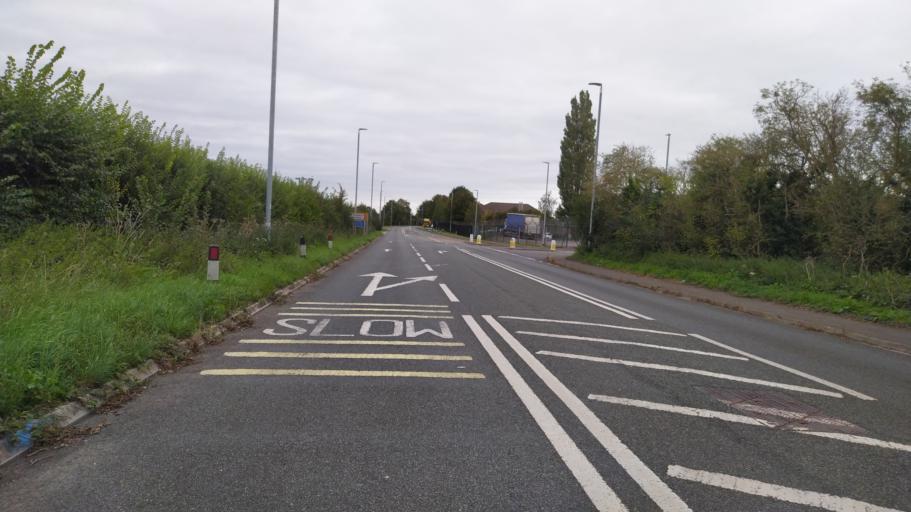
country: GB
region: England
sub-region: Somerset
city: Ilchester
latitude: 51.0122
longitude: -2.6552
